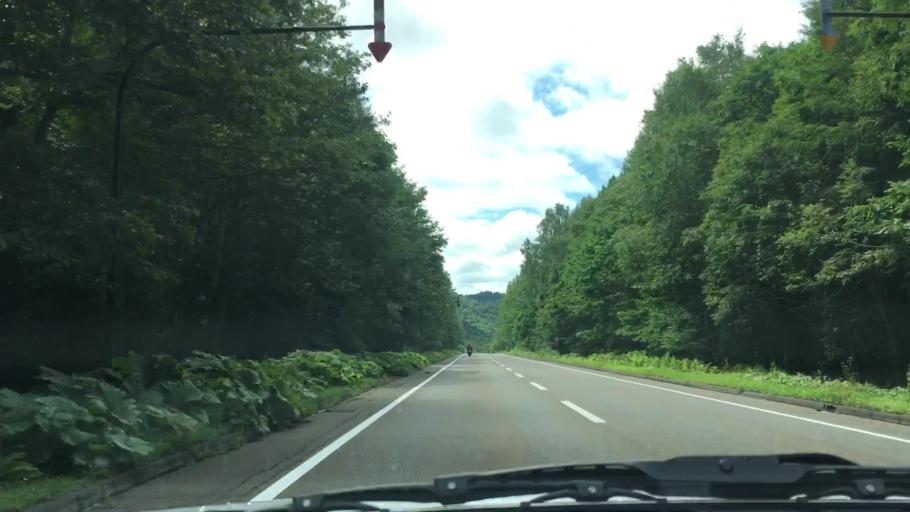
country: JP
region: Hokkaido
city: Kitami
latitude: 43.3980
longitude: 143.9258
